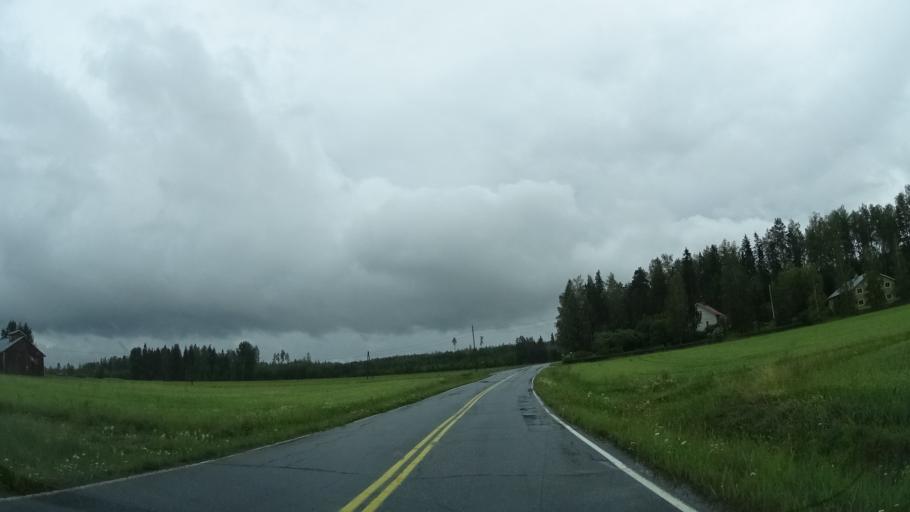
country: FI
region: Haeme
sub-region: Forssa
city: Humppila
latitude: 60.9956
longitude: 23.2539
